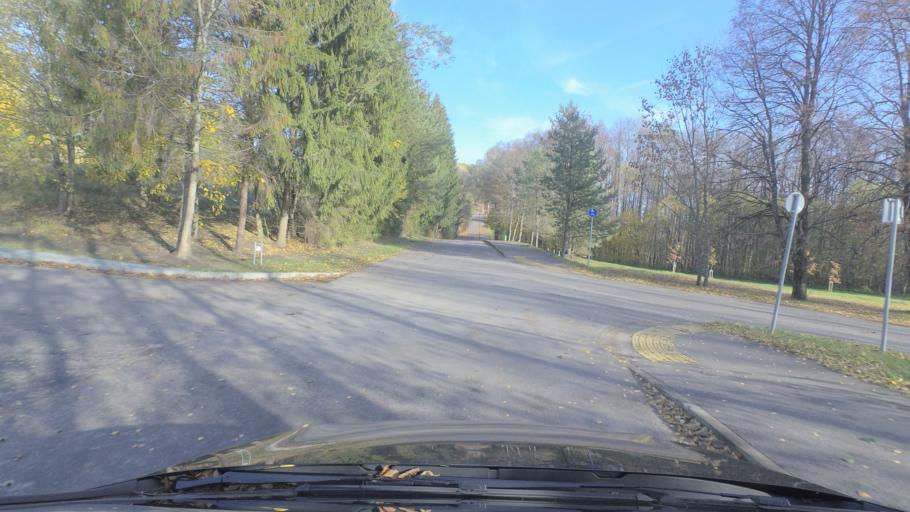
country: LT
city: Ignalina
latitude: 55.3373
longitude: 26.1482
